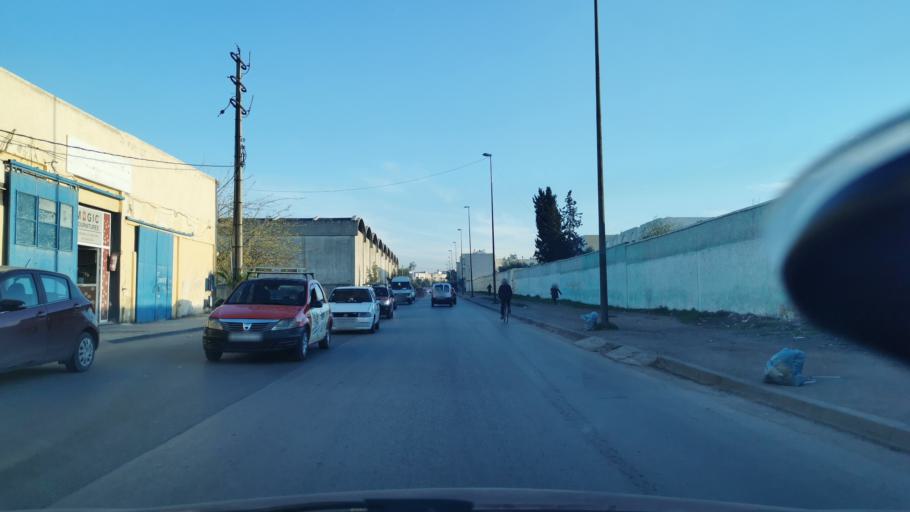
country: MA
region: Fes-Boulemane
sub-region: Fes
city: Fes
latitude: 34.0238
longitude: -4.9844
